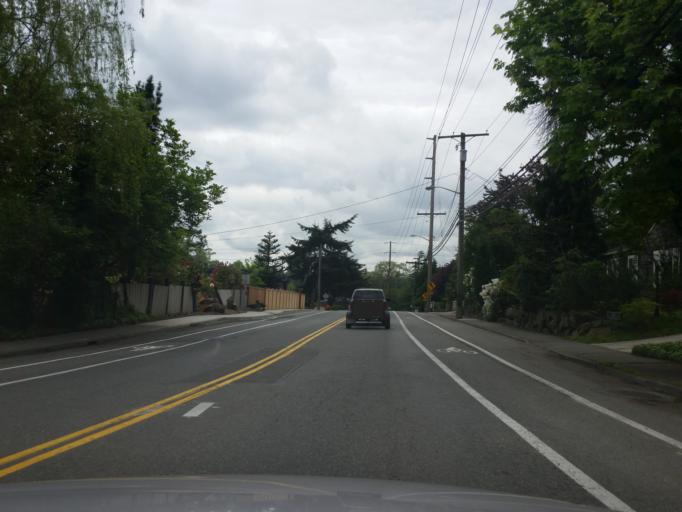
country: US
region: Washington
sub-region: King County
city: Kirkland
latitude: 47.6737
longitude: -122.1963
